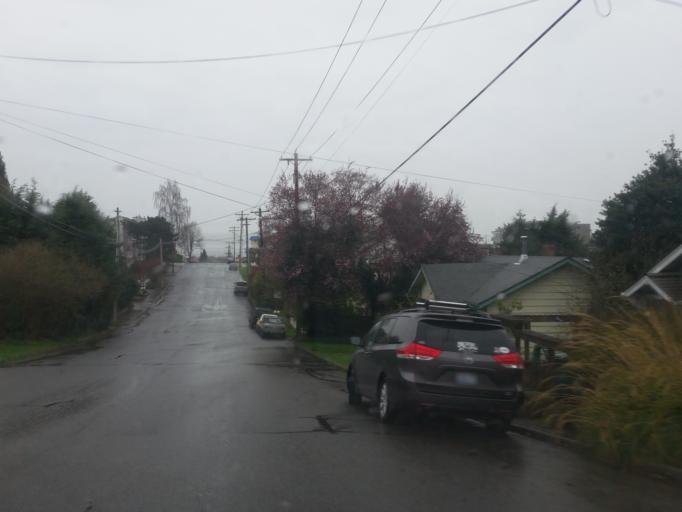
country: US
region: Washington
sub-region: Snohomish County
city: Edmonds
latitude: 47.8074
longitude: -122.3724
